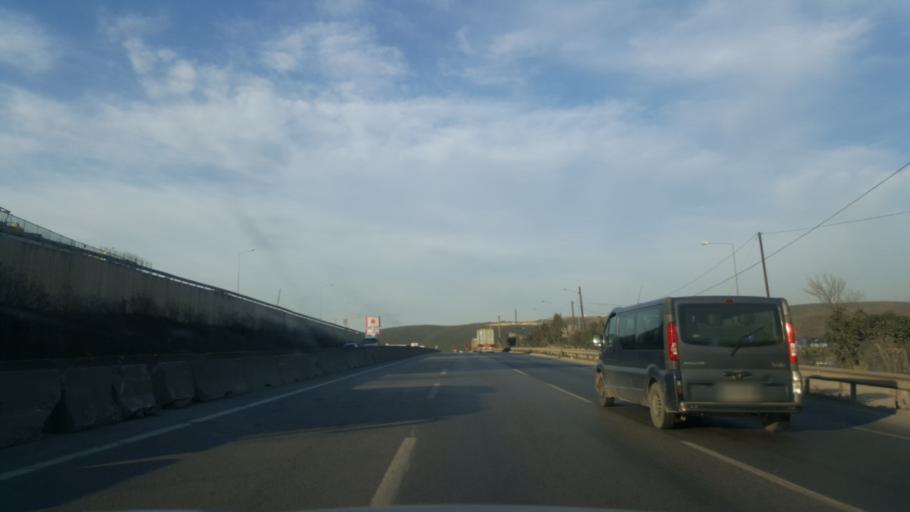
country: TR
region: Kocaeli
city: Tavsanli
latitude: 40.7990
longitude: 29.5251
